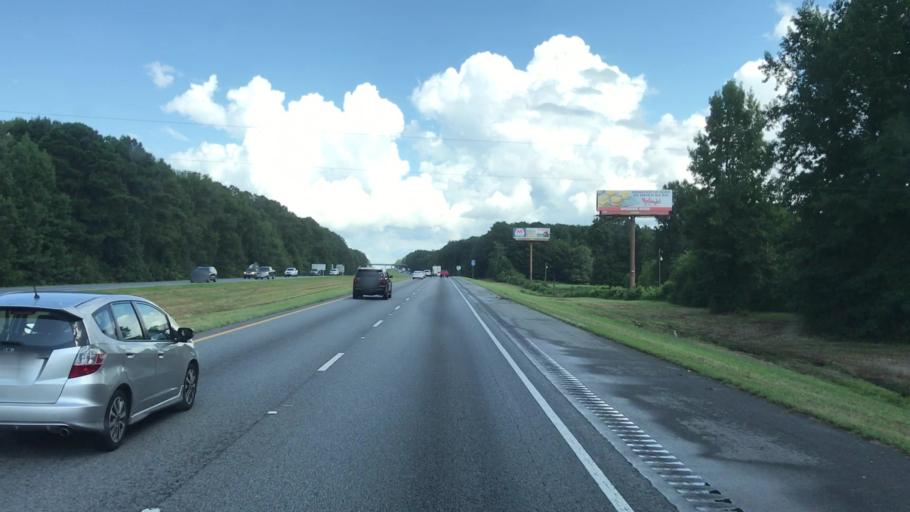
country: US
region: Georgia
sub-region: Walton County
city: Social Circle
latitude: 33.5903
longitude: -83.6229
